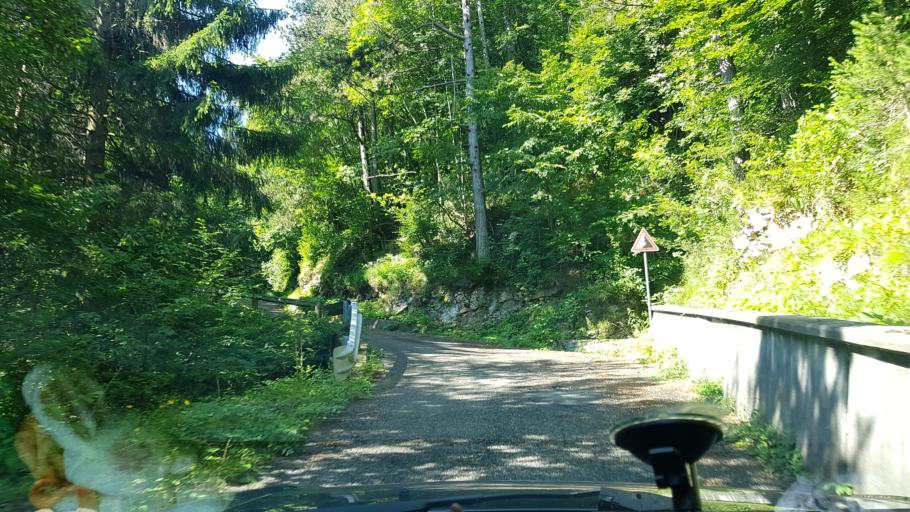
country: IT
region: Friuli Venezia Giulia
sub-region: Provincia di Udine
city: Dogna
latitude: 46.4471
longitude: 13.3094
